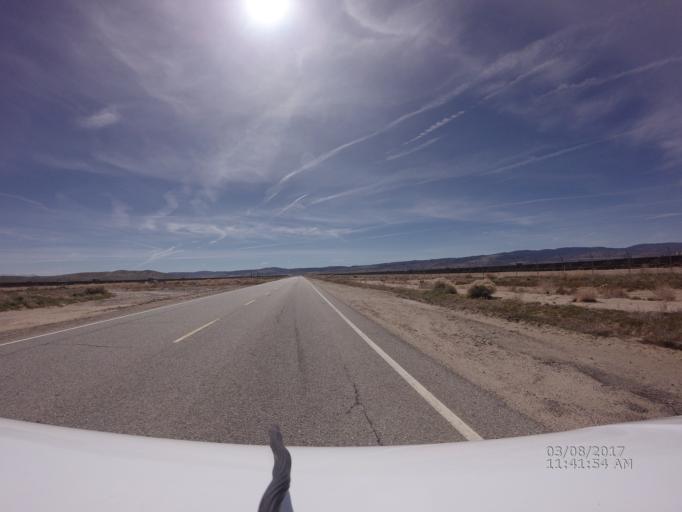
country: US
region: California
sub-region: Los Angeles County
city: Green Valley
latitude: 34.7844
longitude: -118.4314
